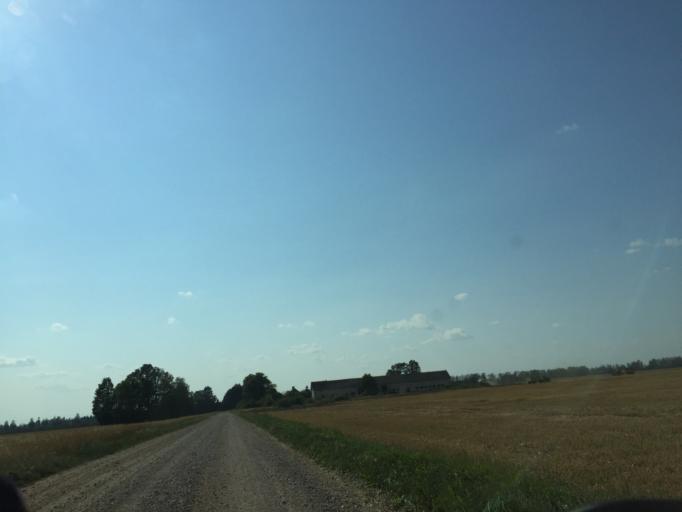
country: LV
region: Jelgava
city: Jelgava
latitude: 56.4552
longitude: 23.7090
